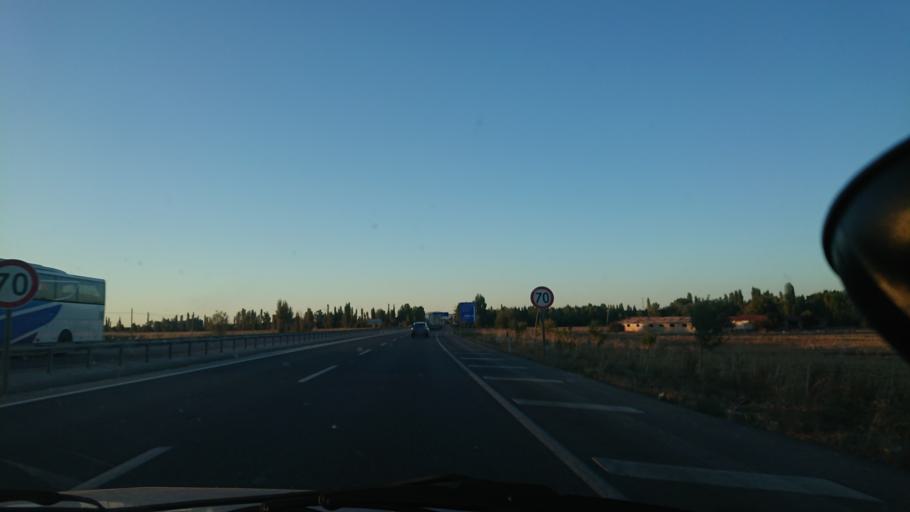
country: TR
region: Eskisehir
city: Mahmudiye
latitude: 39.5647
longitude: 30.9148
